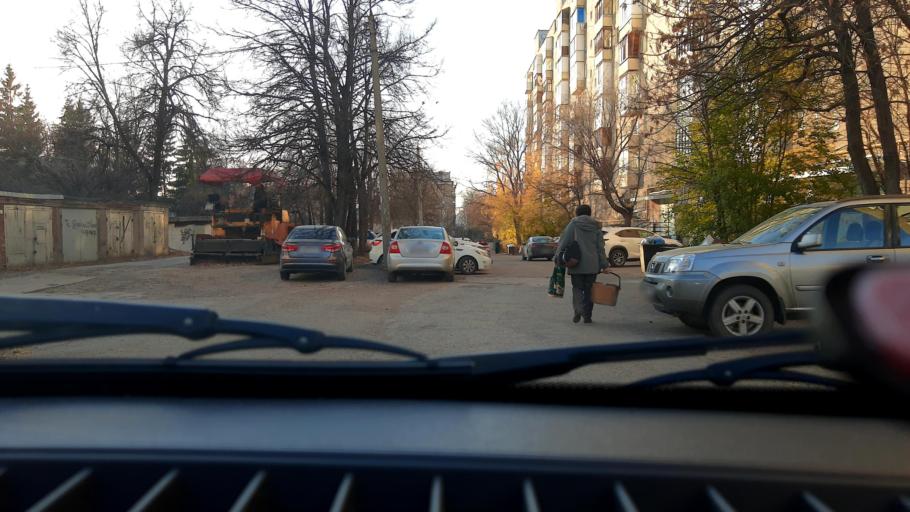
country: RU
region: Bashkortostan
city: Ufa
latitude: 54.7396
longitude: 56.0271
